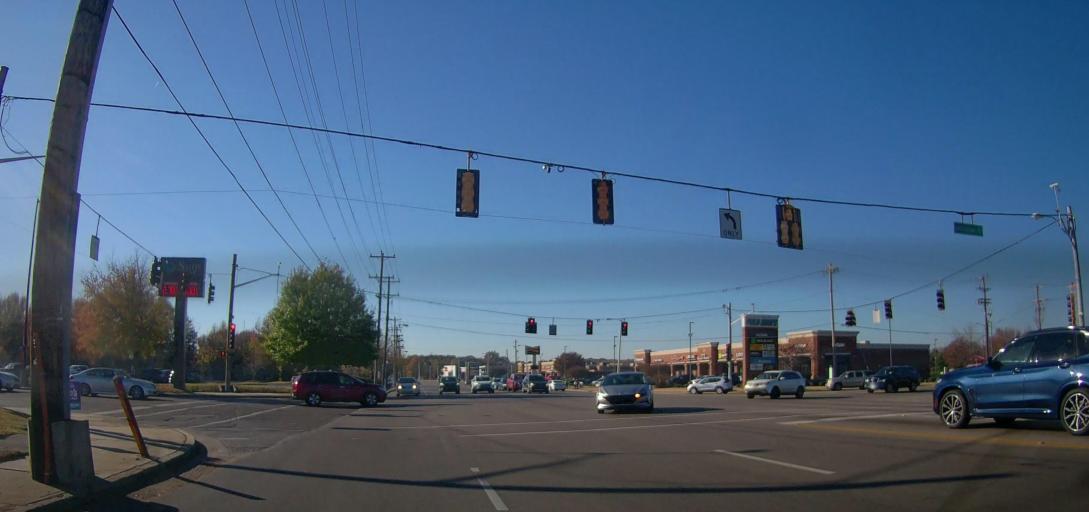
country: US
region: Tennessee
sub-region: Shelby County
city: Germantown
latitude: 35.0496
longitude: -89.8120
